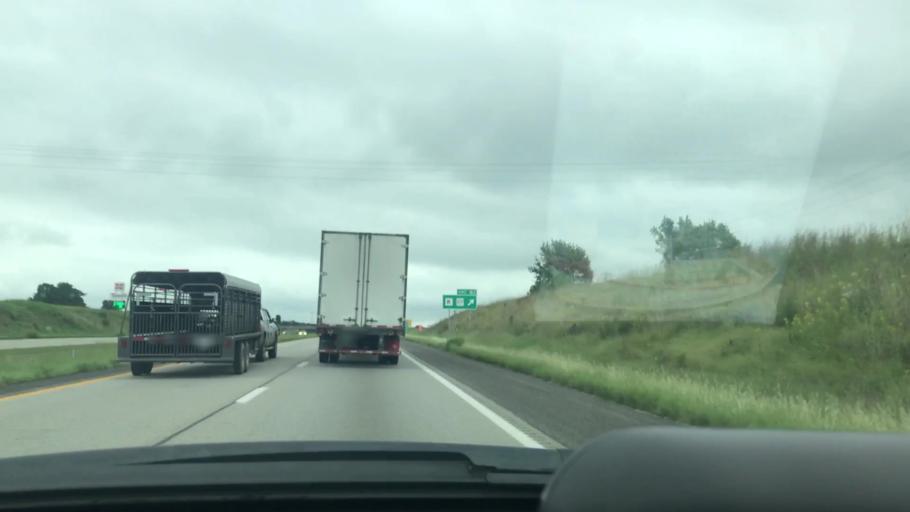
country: US
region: Missouri
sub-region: Greene County
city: Republic
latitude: 37.1859
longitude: -93.5742
